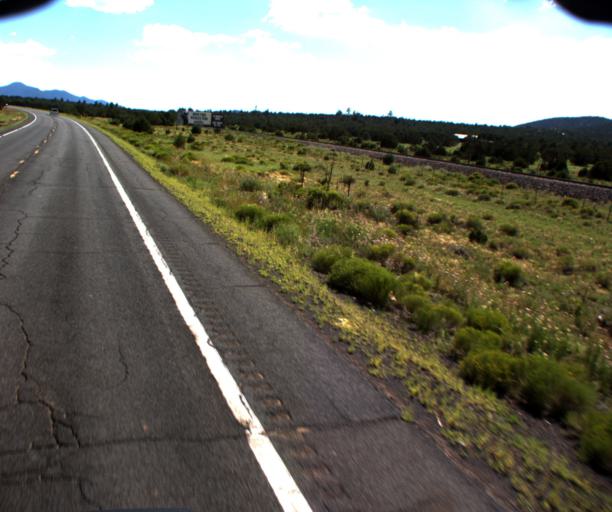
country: US
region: Arizona
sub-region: Coconino County
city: Williams
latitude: 35.3633
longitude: -112.1664
